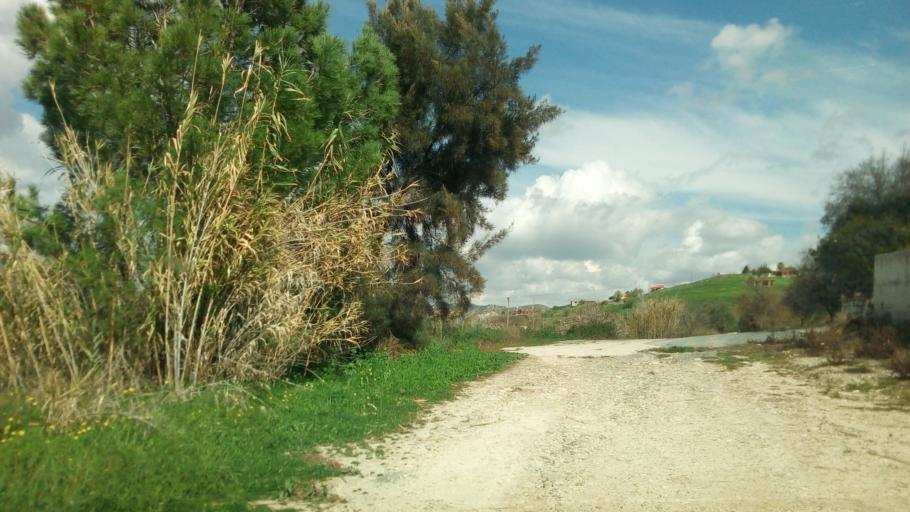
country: CY
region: Pafos
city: Mesogi
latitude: 34.7703
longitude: 32.5827
